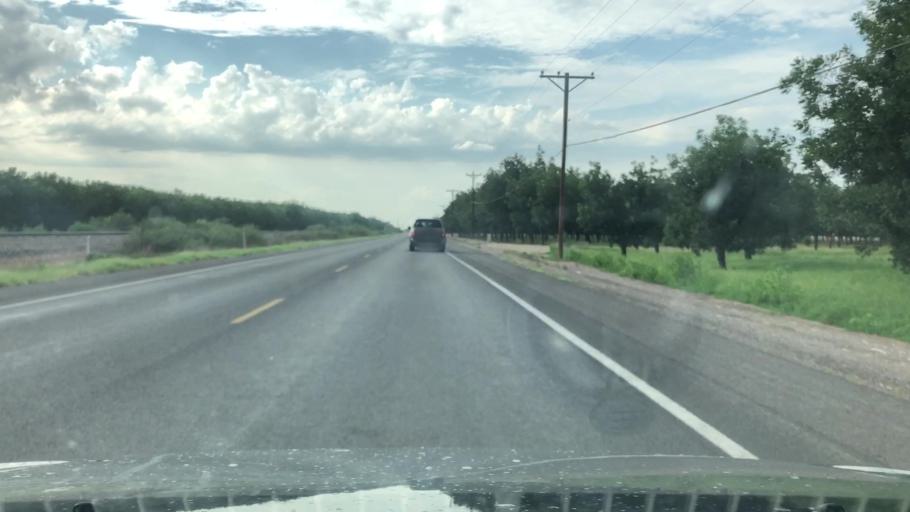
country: US
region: New Mexico
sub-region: Dona Ana County
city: Mesquite
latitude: 32.2118
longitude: -106.7264
